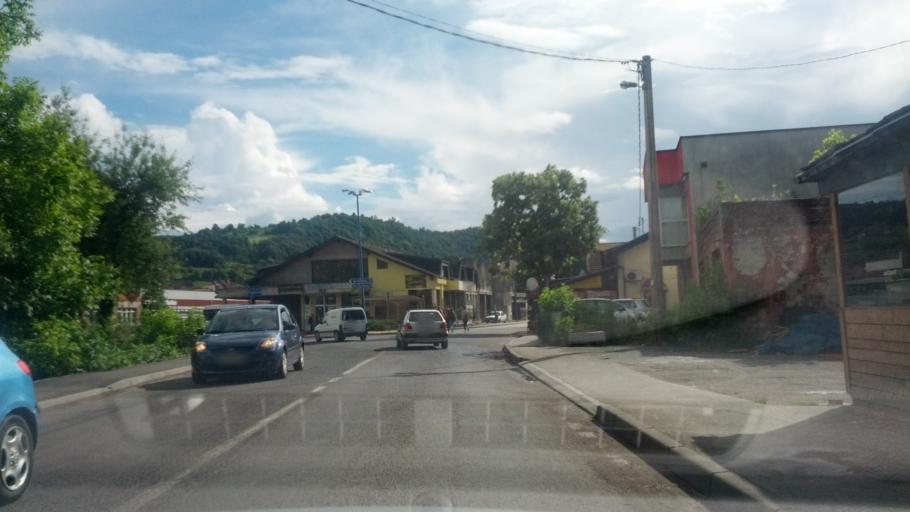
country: BA
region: Federation of Bosnia and Herzegovina
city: Bosanska Krupa
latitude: 44.8868
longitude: 16.1513
